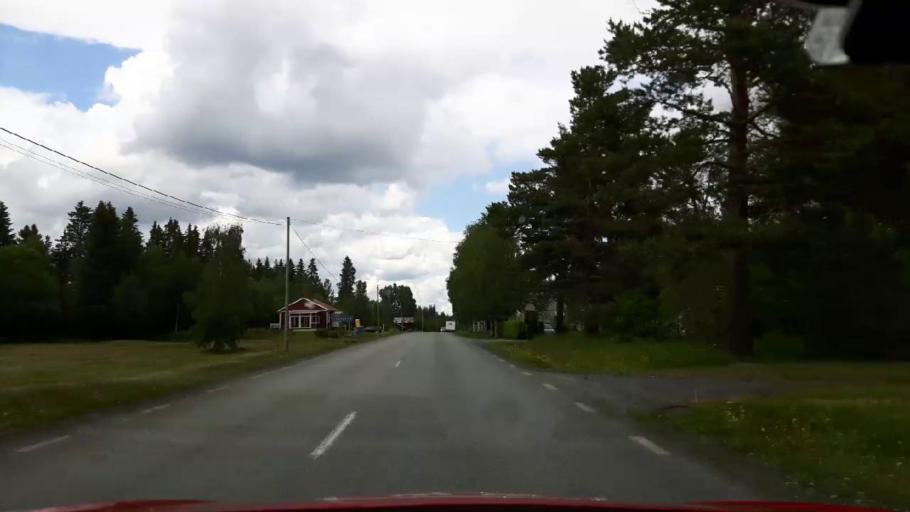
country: SE
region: Jaemtland
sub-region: Krokoms Kommun
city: Krokom
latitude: 63.5175
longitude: 14.2314
